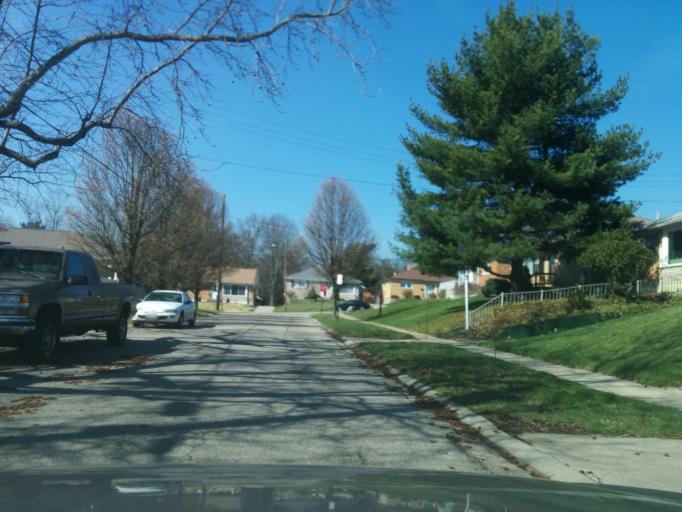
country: US
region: Ohio
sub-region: Hamilton County
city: Monfort Heights
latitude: 39.1996
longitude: -84.5911
